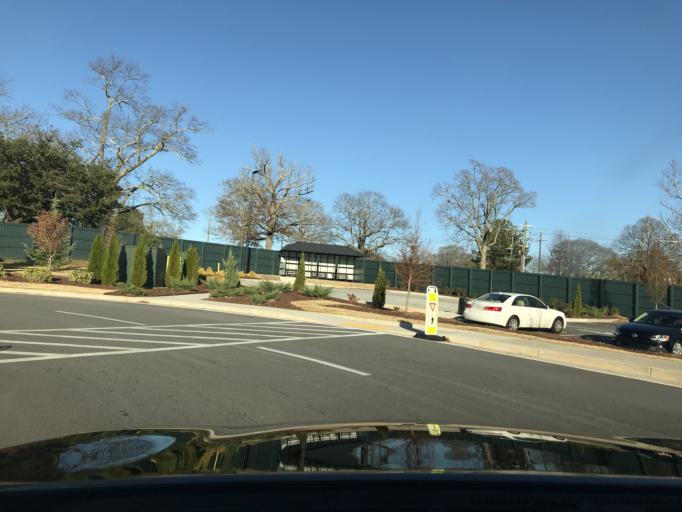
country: US
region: Georgia
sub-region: Fulton County
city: East Point
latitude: 33.7029
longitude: -84.4300
